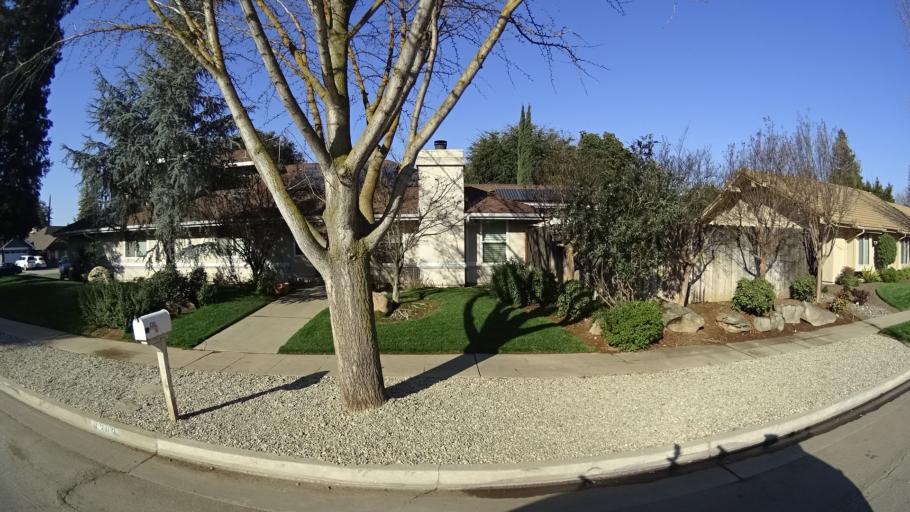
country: US
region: California
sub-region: Fresno County
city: Clovis
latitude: 36.8577
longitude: -119.7922
